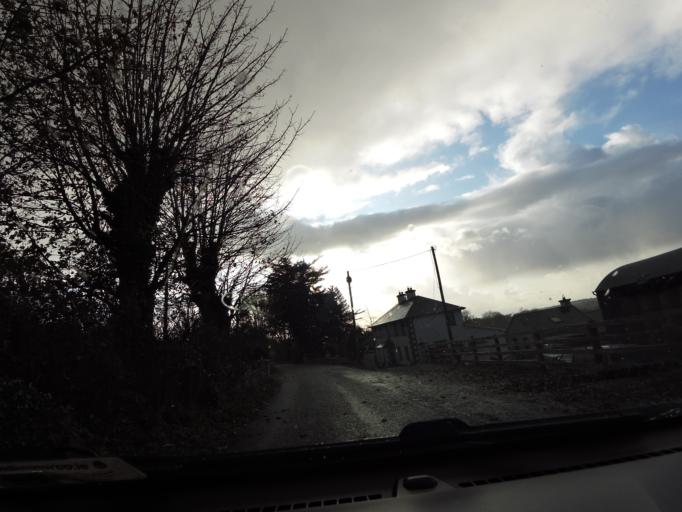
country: IE
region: Munster
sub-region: North Tipperary
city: Newport
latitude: 52.6936
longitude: -8.3984
